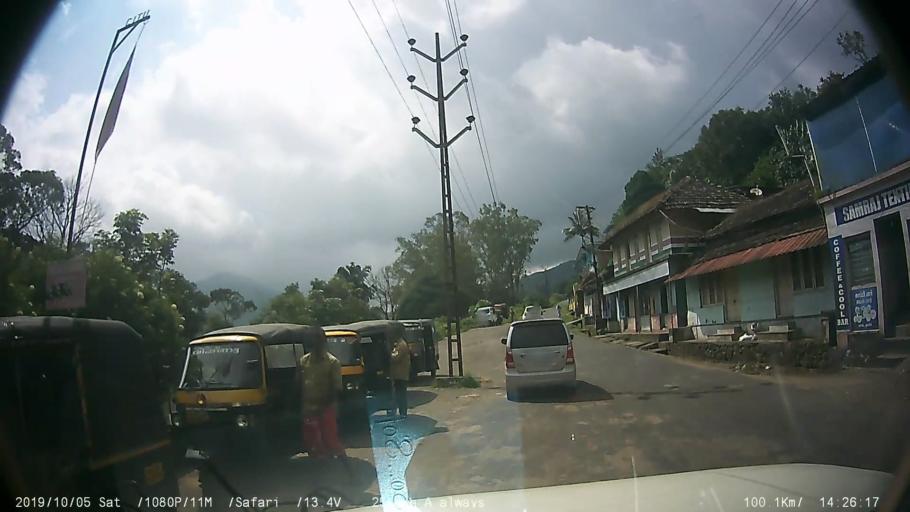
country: IN
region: Kerala
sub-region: Kottayam
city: Erattupetta
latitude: 9.5985
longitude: 76.9682
